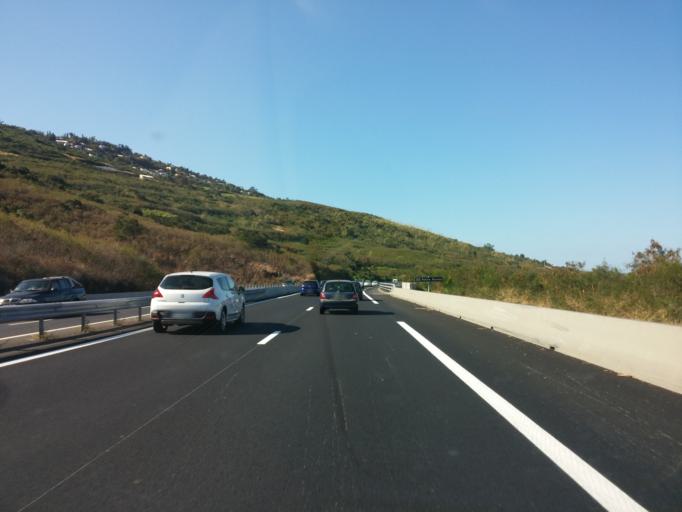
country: RE
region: Reunion
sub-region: Reunion
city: Trois-Bassins
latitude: -21.1317
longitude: 55.2835
